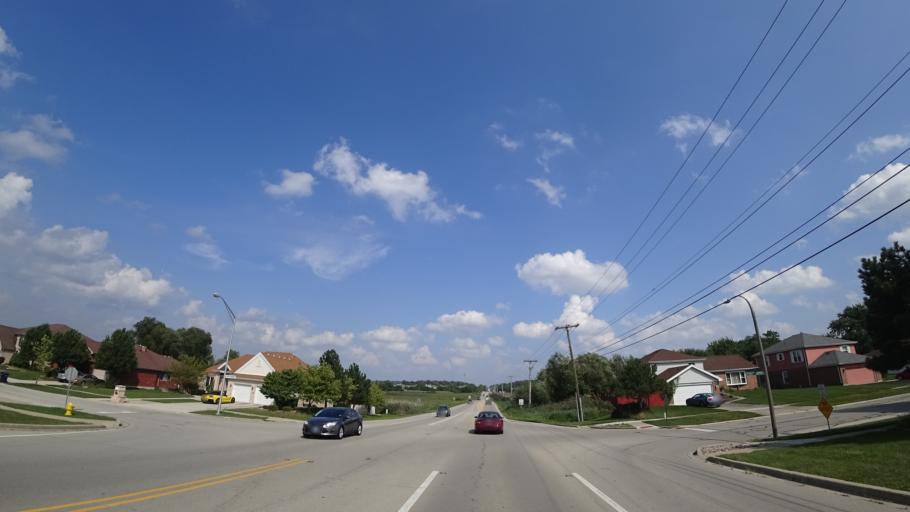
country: US
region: Illinois
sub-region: Will County
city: Goodings Grove
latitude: 41.6296
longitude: -87.9018
